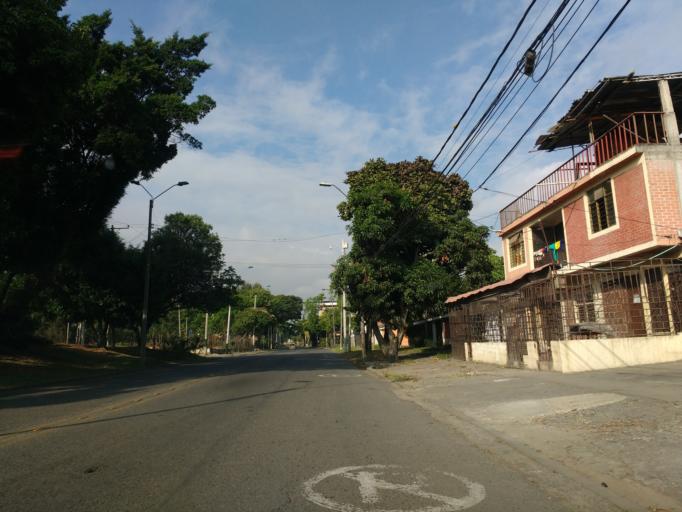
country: CO
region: Valle del Cauca
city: Cali
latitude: 3.4738
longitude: -76.5153
